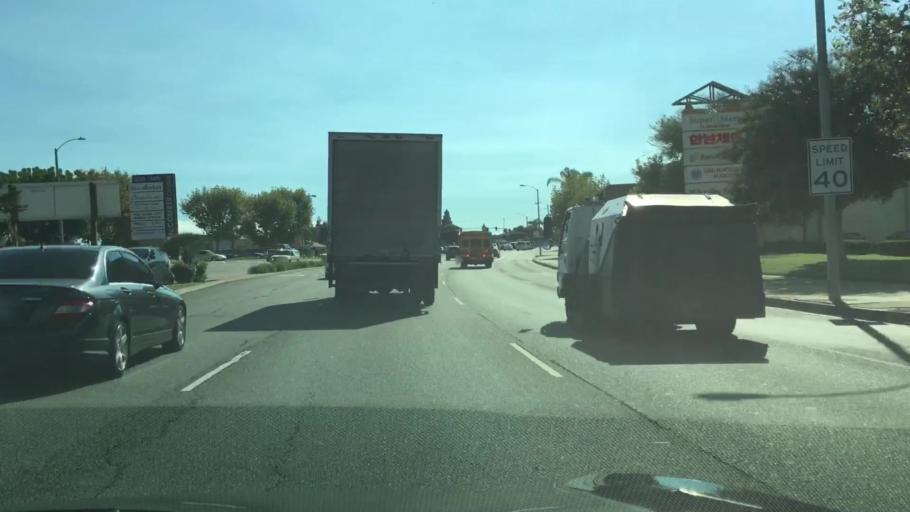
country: US
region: California
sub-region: Orange County
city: Buena Park
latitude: 33.8837
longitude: -117.9962
